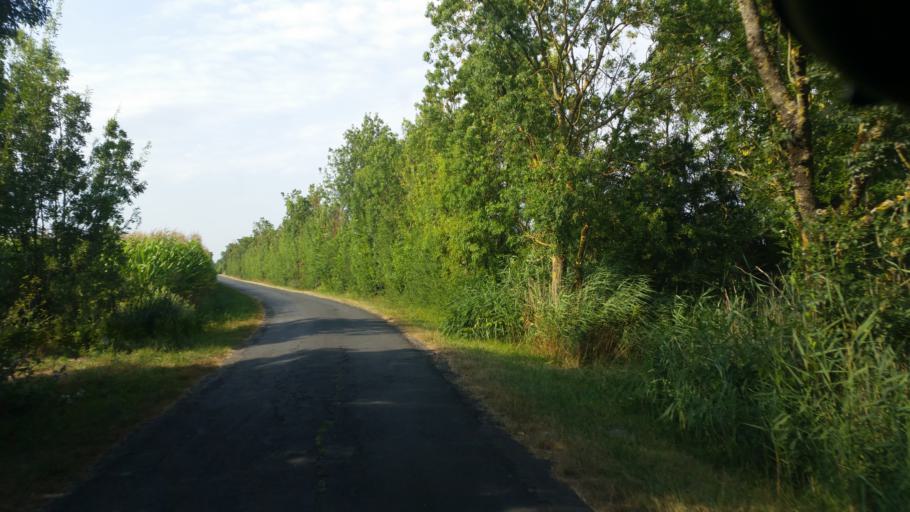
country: FR
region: Poitou-Charentes
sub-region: Departement de la Charente-Maritime
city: Saint-Jean-de-Liversay
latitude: 46.3093
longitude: -0.8962
